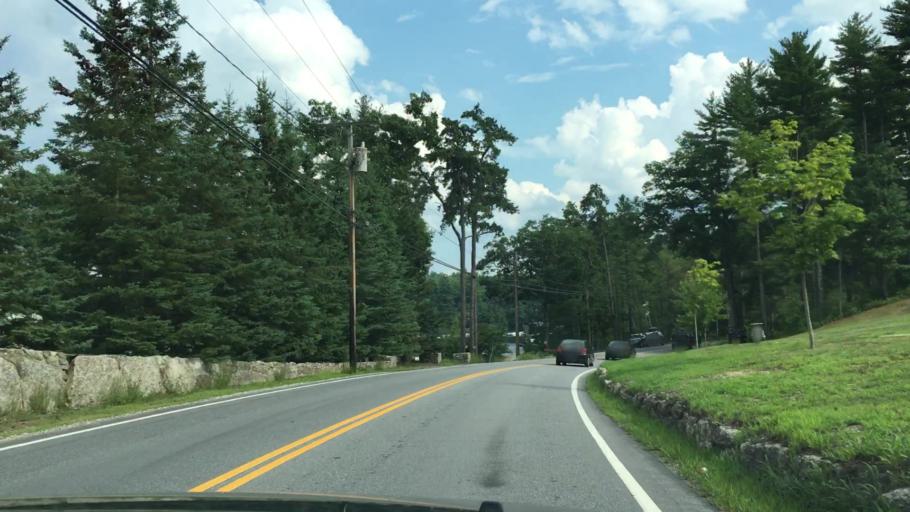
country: US
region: New Hampshire
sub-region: Belknap County
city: Gilford
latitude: 43.5986
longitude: -71.4316
